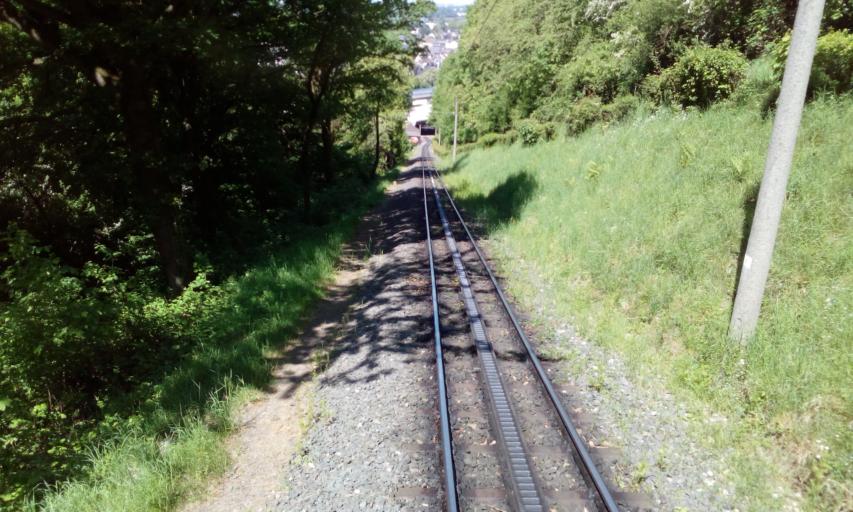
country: DE
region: North Rhine-Westphalia
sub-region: Regierungsbezirk Koln
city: Konigswinter
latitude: 50.6728
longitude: 7.2008
